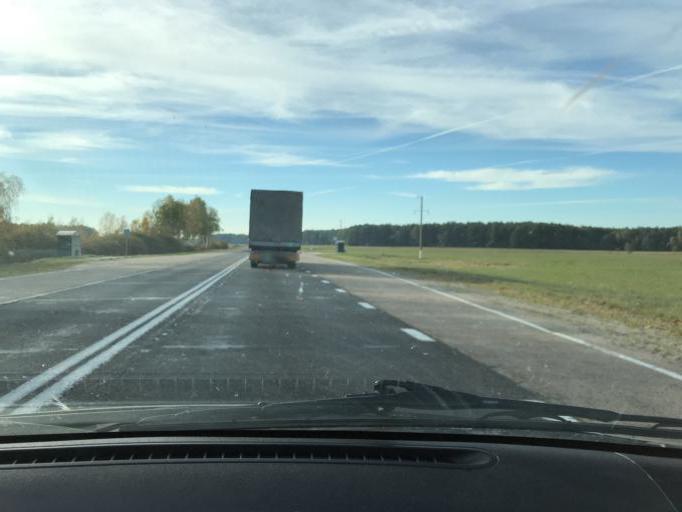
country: BY
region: Brest
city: Lahishyn
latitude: 52.1531
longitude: 25.8200
